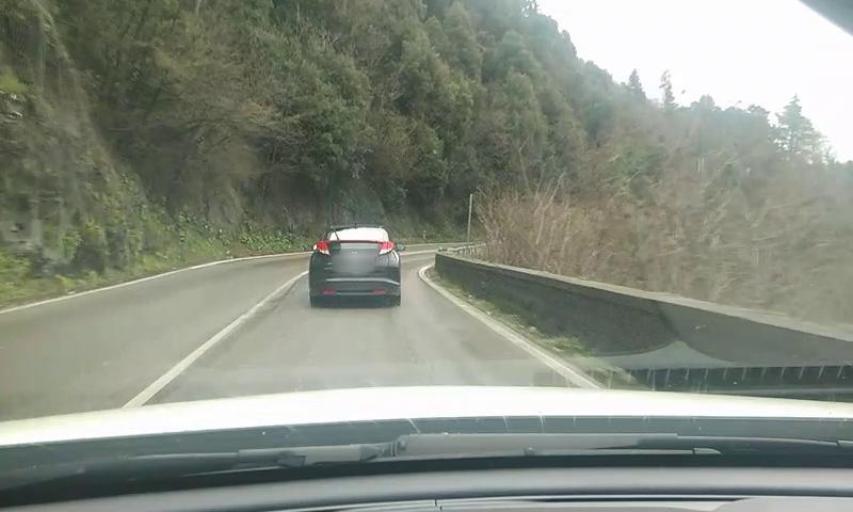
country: IT
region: Tuscany
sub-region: Provincia di Prato
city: Vaiano
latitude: 43.9299
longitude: 11.1265
